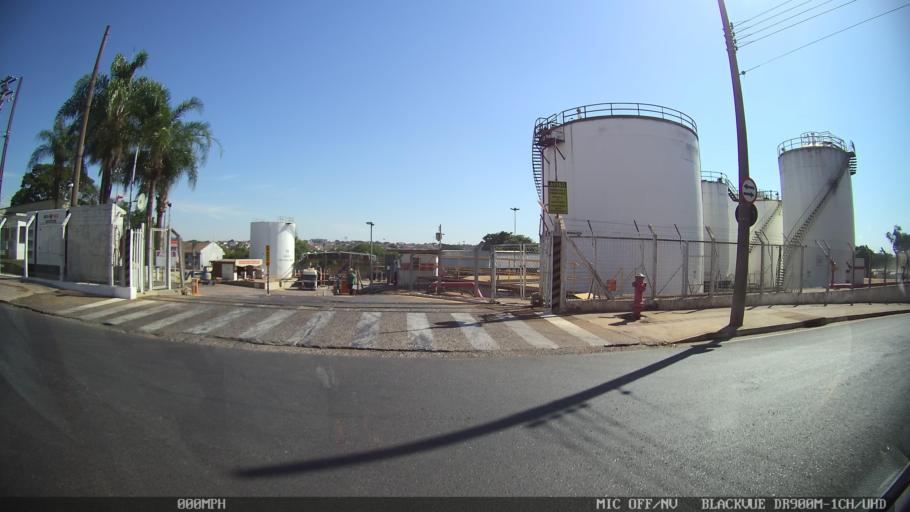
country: BR
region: Sao Paulo
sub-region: Sao Jose Do Rio Preto
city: Sao Jose do Rio Preto
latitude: -20.7927
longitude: -49.3881
